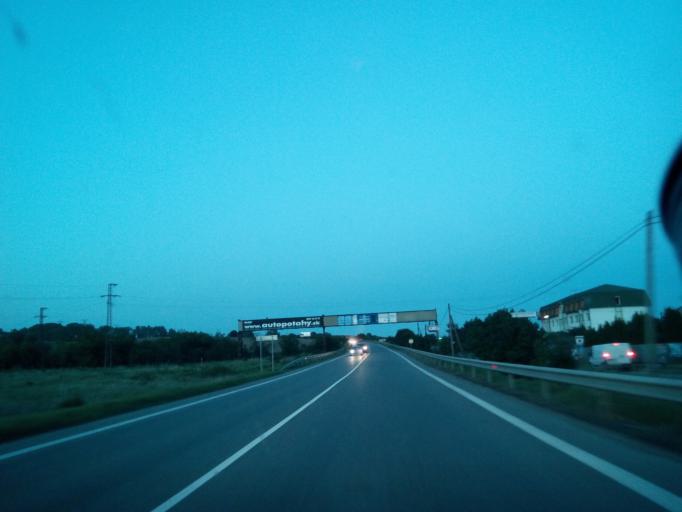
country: SK
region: Banskobystricky
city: Rimavska Sobota
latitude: 48.3922
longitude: 20.0082
